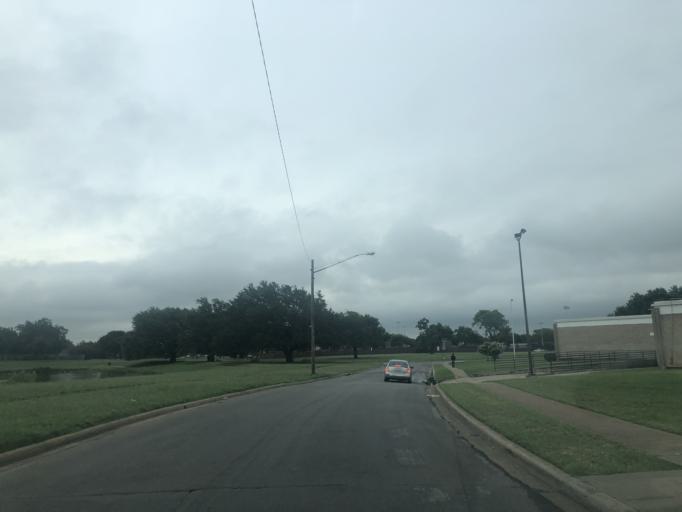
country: US
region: Texas
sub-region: Dallas County
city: Cockrell Hill
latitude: 32.7814
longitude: -96.8604
